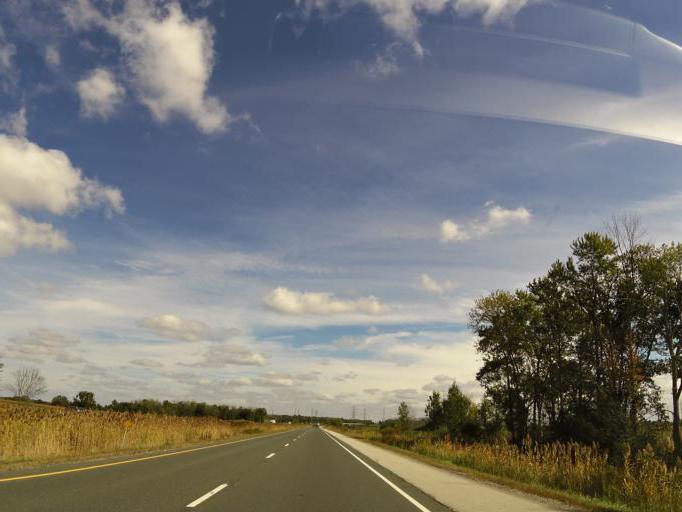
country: CA
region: Ontario
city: London
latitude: 42.9039
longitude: -81.2593
